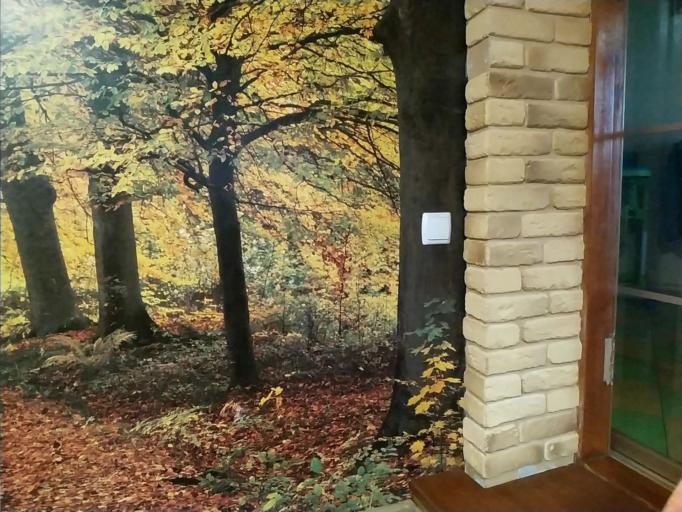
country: RU
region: Smolensk
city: Safonovo
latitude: 55.1944
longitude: 33.1362
